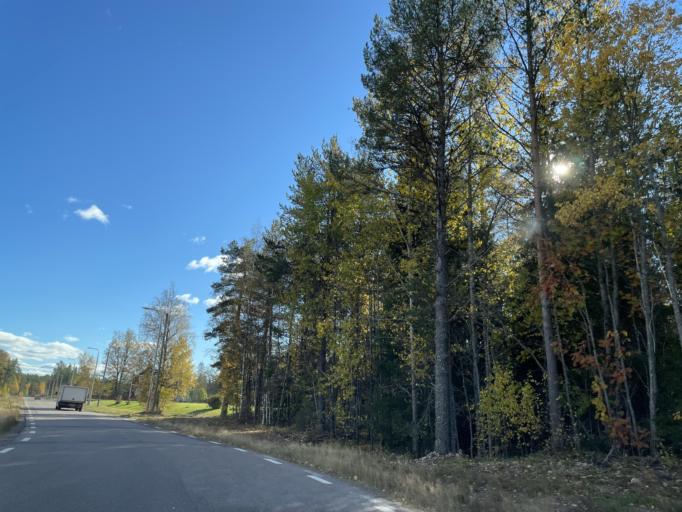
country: SE
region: Dalarna
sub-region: Malung-Saelens kommun
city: Malung
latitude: 60.9035
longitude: 13.3725
